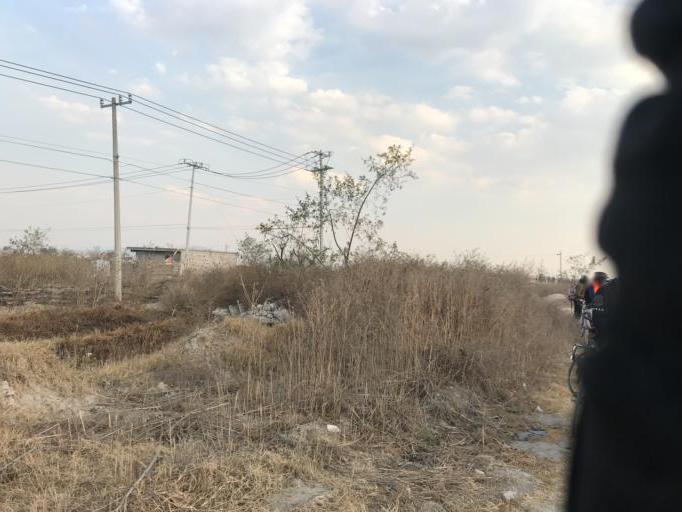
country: MX
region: Mexico
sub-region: Nextlalpan
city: Ex-Hacienda Santa Ines
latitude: 19.6944
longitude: -99.0791
